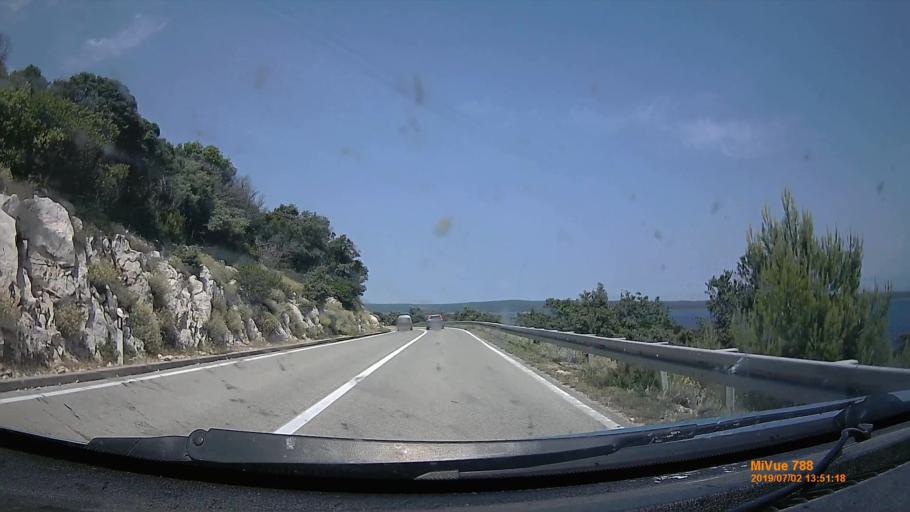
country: HR
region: Primorsko-Goranska
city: Mali Losinj
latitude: 44.6074
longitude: 14.4016
